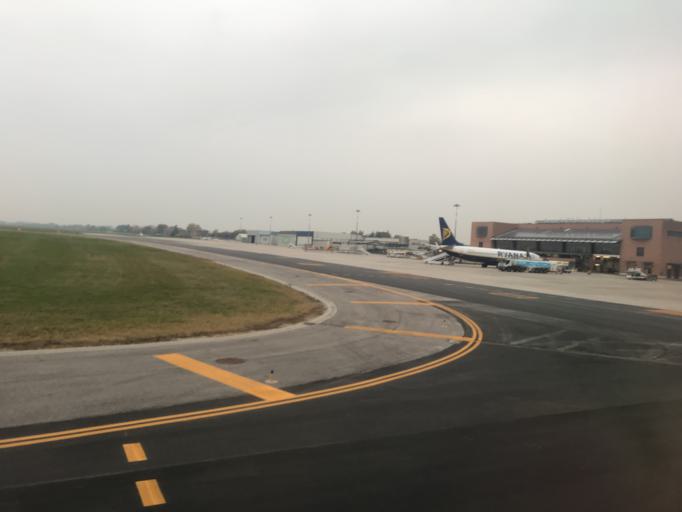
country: IT
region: Veneto
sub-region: Provincia di Treviso
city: Treviso
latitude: 45.6536
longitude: 12.2073
